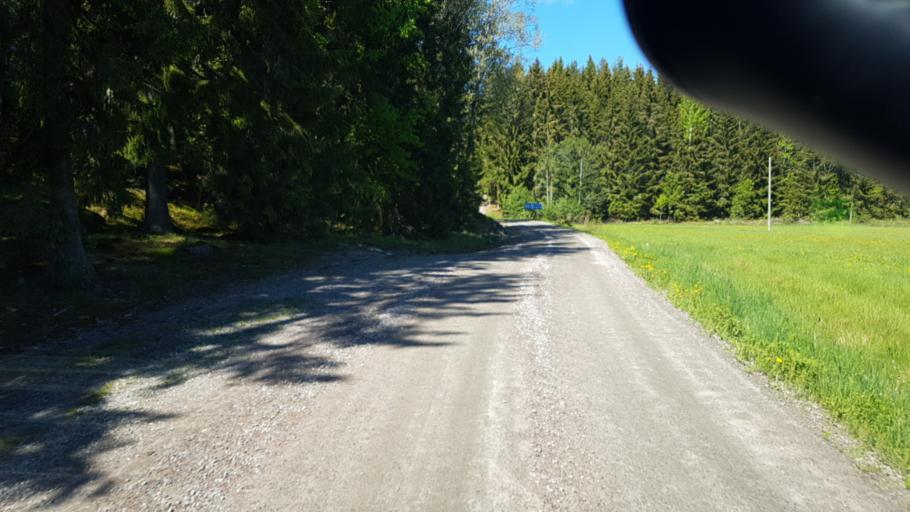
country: SE
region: Vaermland
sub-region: Grums Kommun
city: Grums
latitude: 59.5369
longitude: 12.8818
